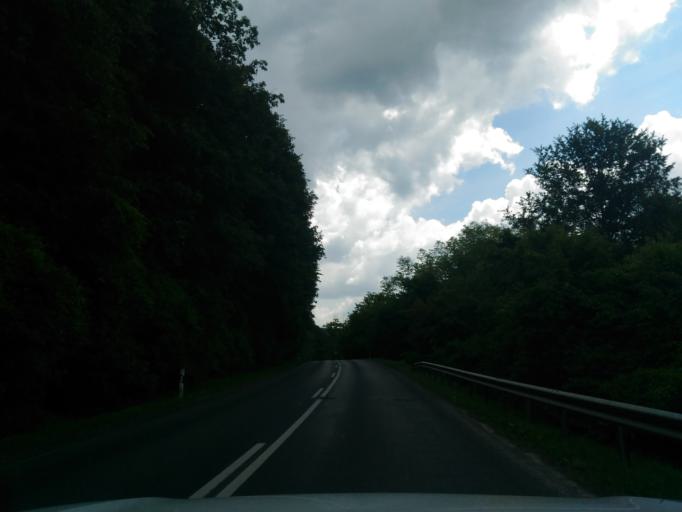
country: HU
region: Baranya
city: Komlo
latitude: 46.1779
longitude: 18.2099
